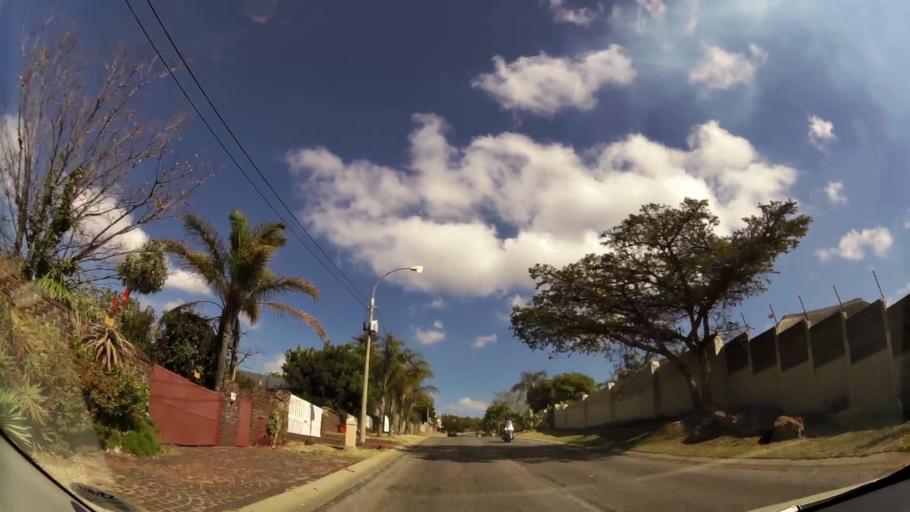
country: ZA
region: Gauteng
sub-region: City of Johannesburg Metropolitan Municipality
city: Roodepoort
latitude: -26.1168
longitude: 27.8417
